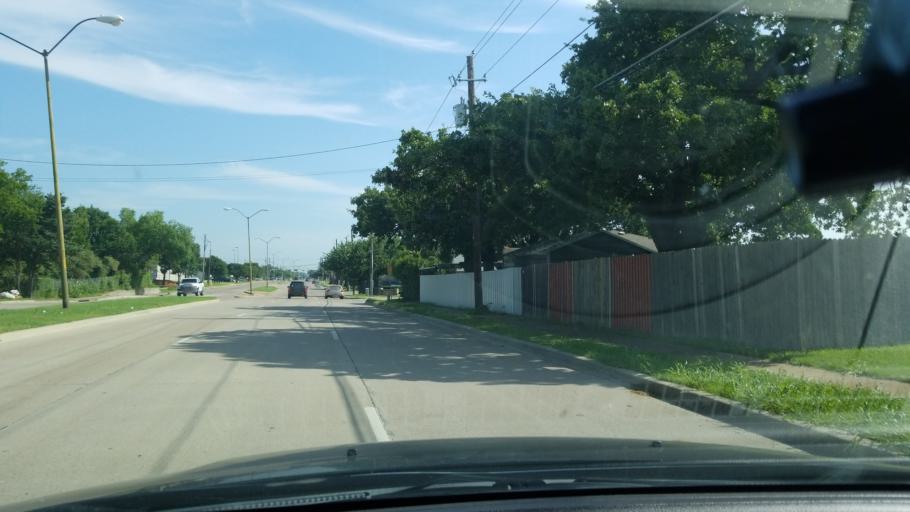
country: US
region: Texas
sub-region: Dallas County
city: Balch Springs
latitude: 32.7302
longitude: -96.6483
